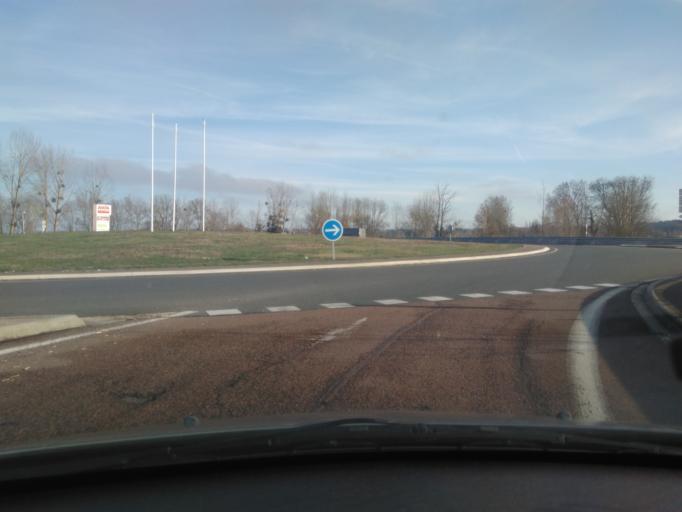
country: FR
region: Bourgogne
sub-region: Departement de la Nievre
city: Magny-Cours
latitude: 46.8731
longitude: 3.1543
